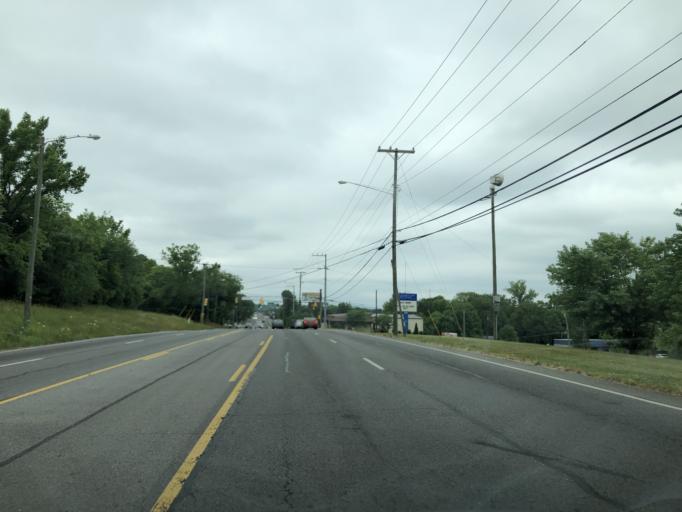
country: US
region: Tennessee
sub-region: Davidson County
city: Goodlettsville
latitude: 36.2787
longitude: -86.7507
